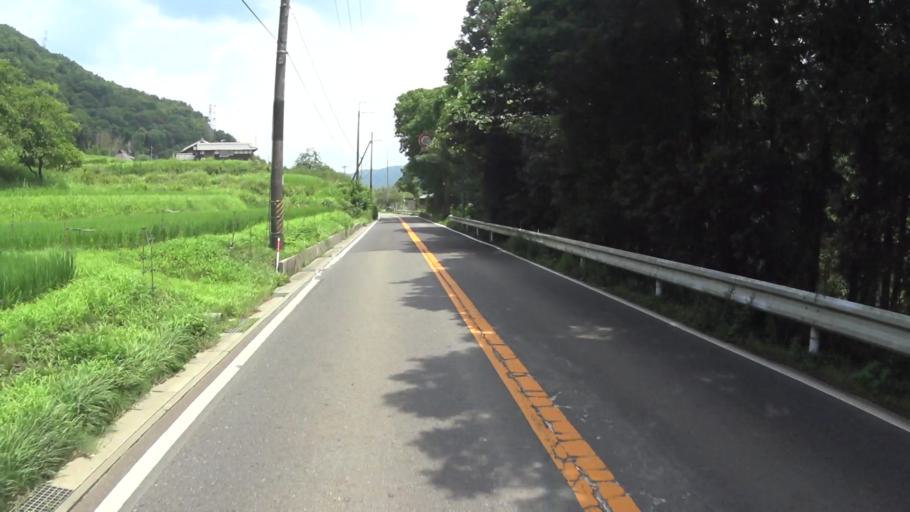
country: JP
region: Nara
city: Nara-shi
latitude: 34.7666
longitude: 135.9073
